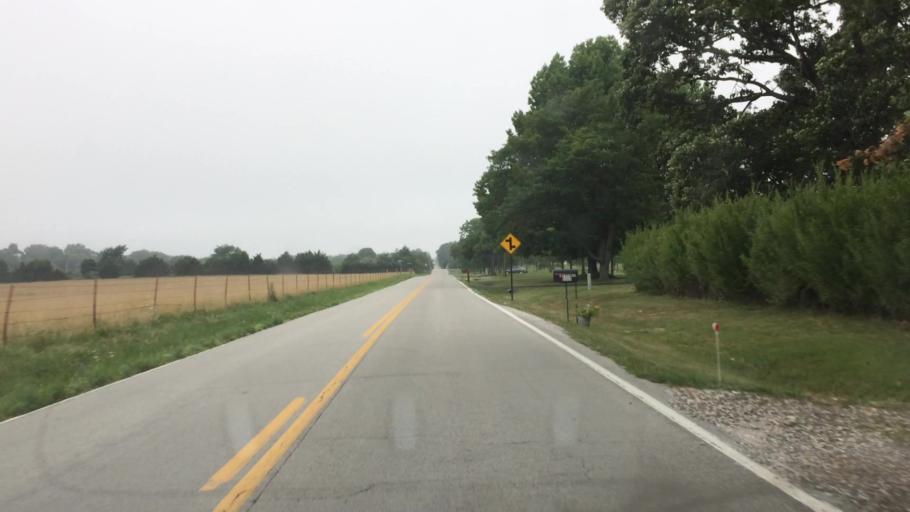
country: US
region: Missouri
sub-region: Greene County
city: Strafford
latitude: 37.2720
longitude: -93.1850
